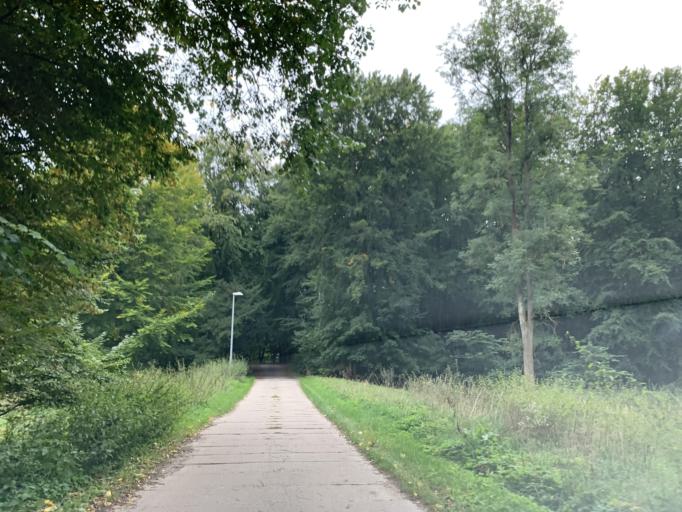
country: DE
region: Mecklenburg-Vorpommern
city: Woldegk
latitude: 53.3350
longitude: 13.6174
